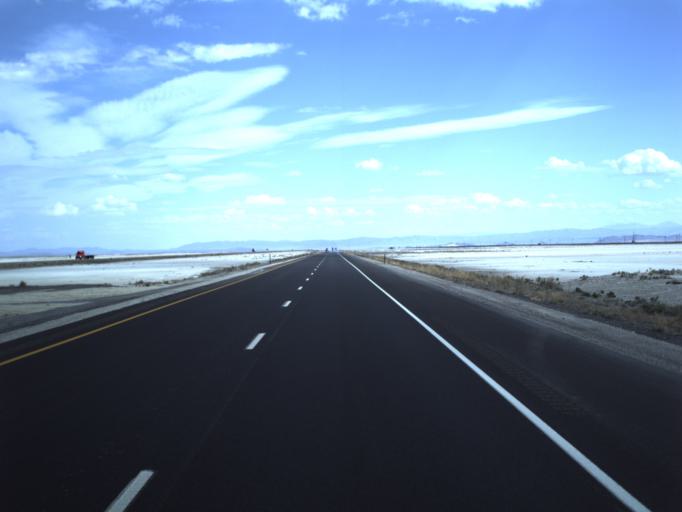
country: US
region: Utah
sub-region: Tooele County
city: Wendover
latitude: 40.7306
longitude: -113.4887
